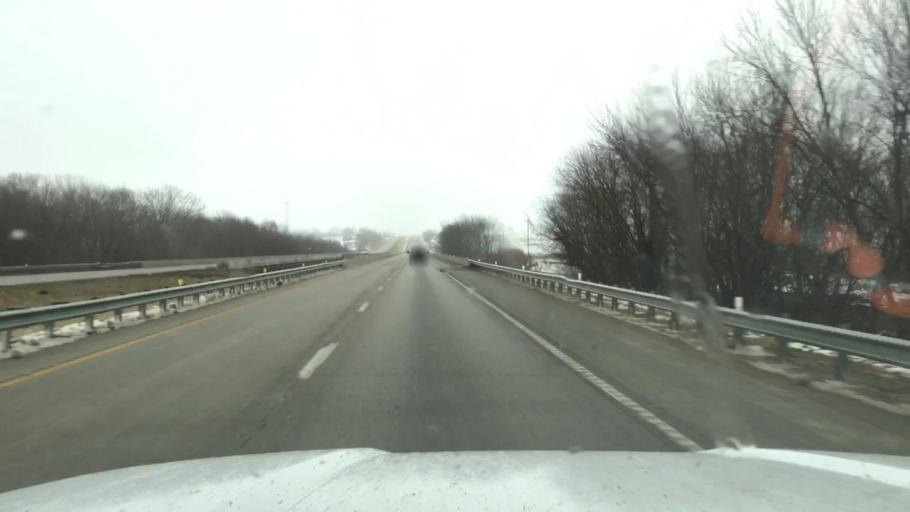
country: US
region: Missouri
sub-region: Clinton County
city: Gower
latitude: 39.7473
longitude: -94.6636
